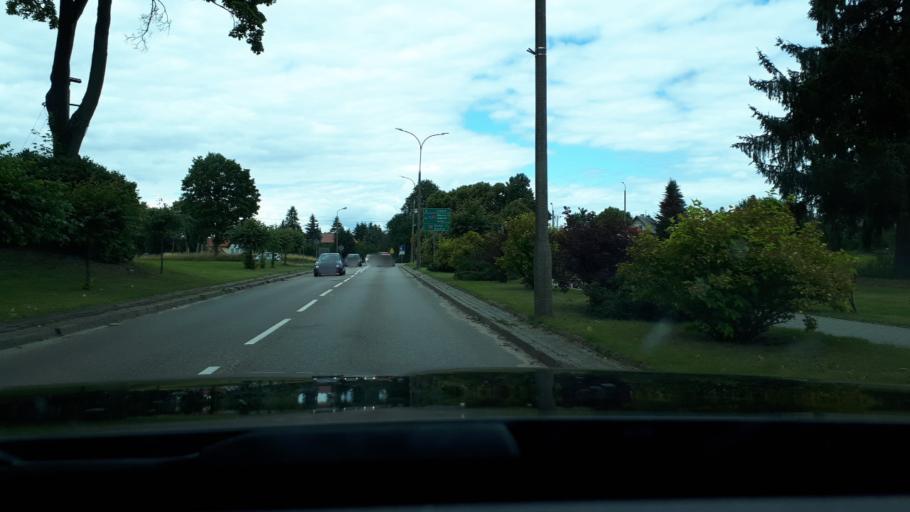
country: PL
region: Warmian-Masurian Voivodeship
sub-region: Powiat olsztynski
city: Olsztynek
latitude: 53.5847
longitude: 20.2845
